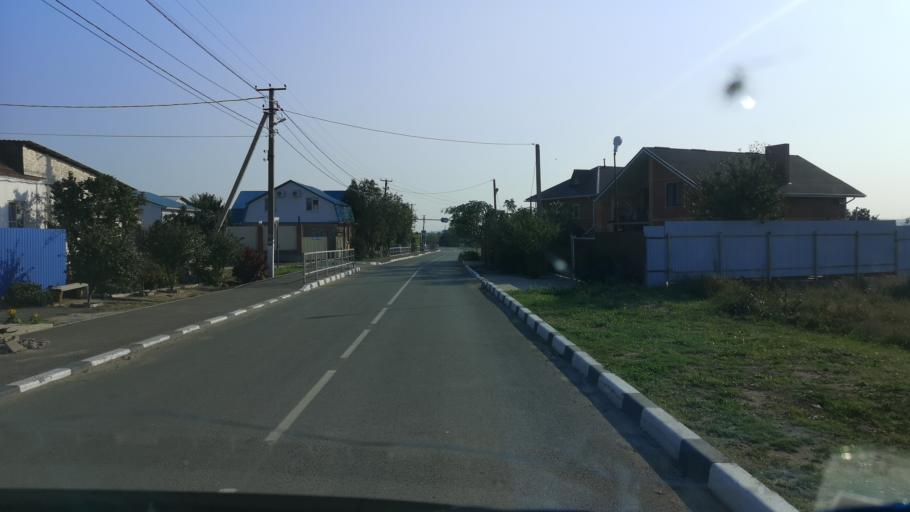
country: RU
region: Krasnodarskiy
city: Taman'
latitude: 45.2135
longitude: 36.6964
